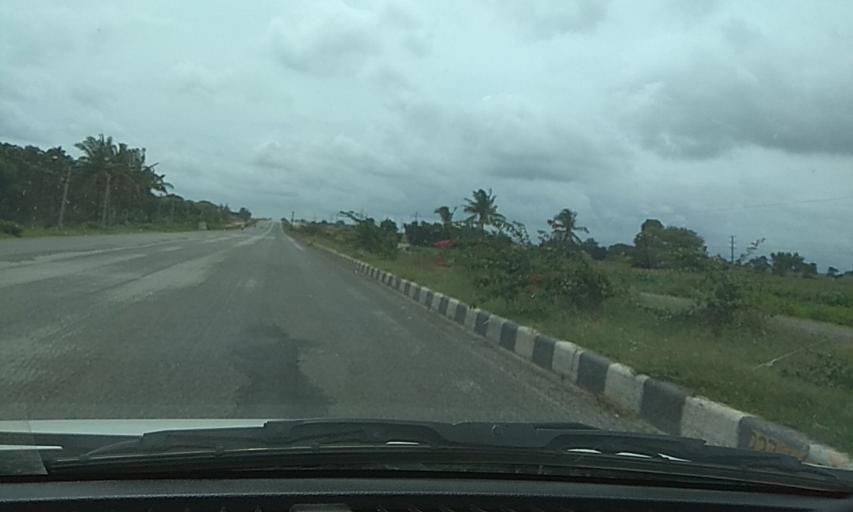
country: IN
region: Karnataka
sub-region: Davanagere
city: Mayakonda
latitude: 14.3325
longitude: 76.2179
